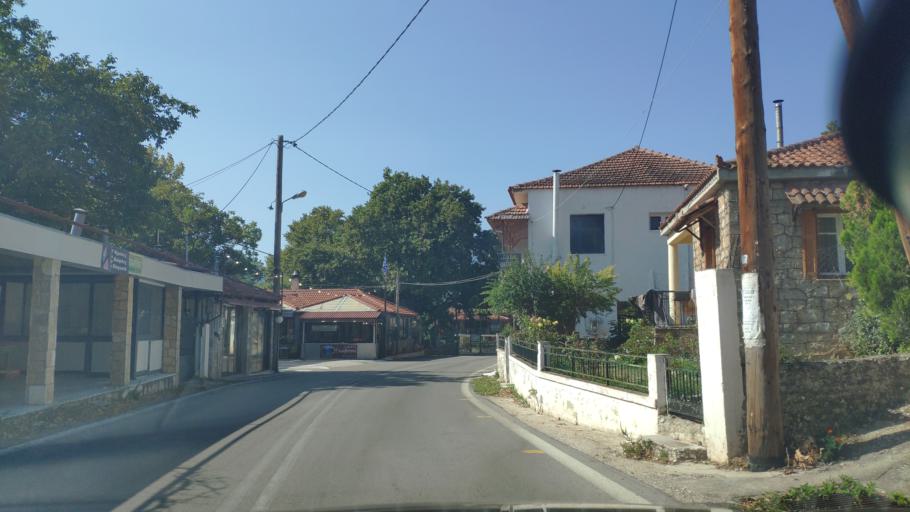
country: GR
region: Peloponnese
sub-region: Nomos Korinthias
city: Nemea
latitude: 37.8700
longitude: 22.4648
